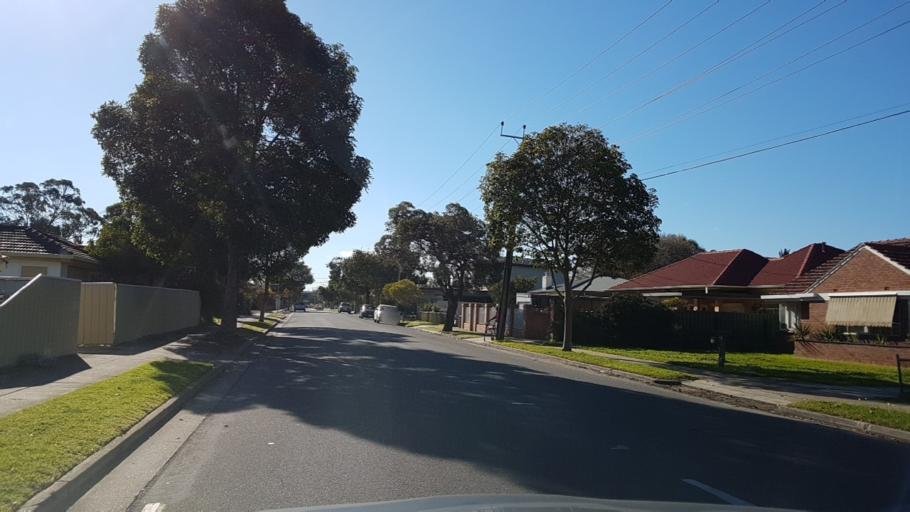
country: AU
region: South Australia
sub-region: City of West Torrens
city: Plympton
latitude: -34.9638
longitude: 138.5453
